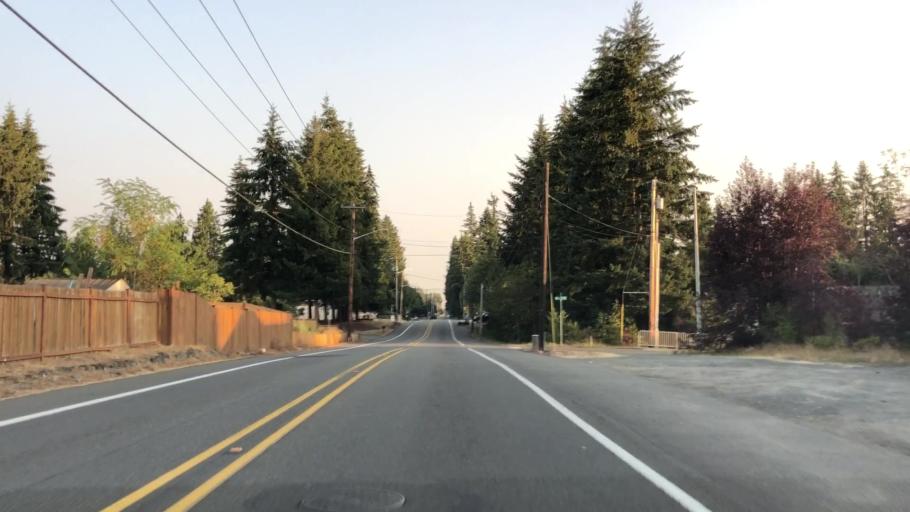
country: US
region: Washington
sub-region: Snohomish County
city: Marysville
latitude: 48.1027
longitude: -122.1622
